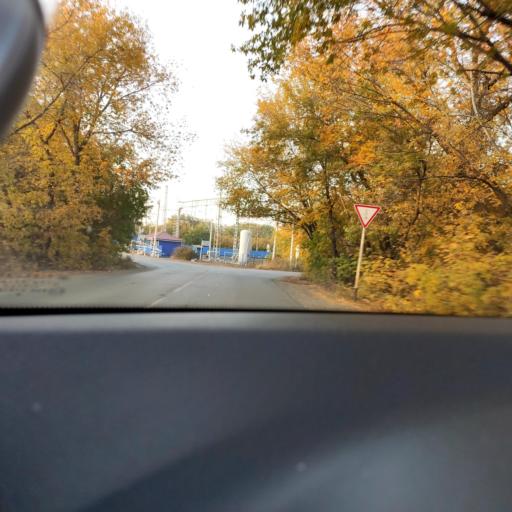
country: RU
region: Samara
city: Smyshlyayevka
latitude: 53.2524
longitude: 50.3684
